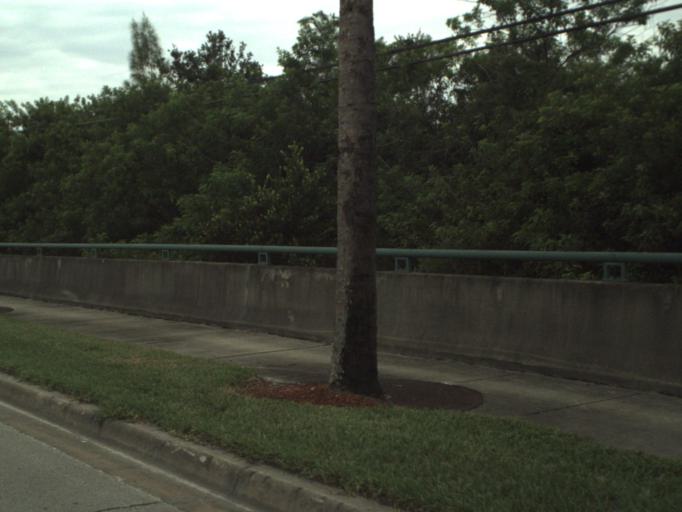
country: US
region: Florida
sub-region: Palm Beach County
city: Wellington
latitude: 26.6813
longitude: -80.2380
